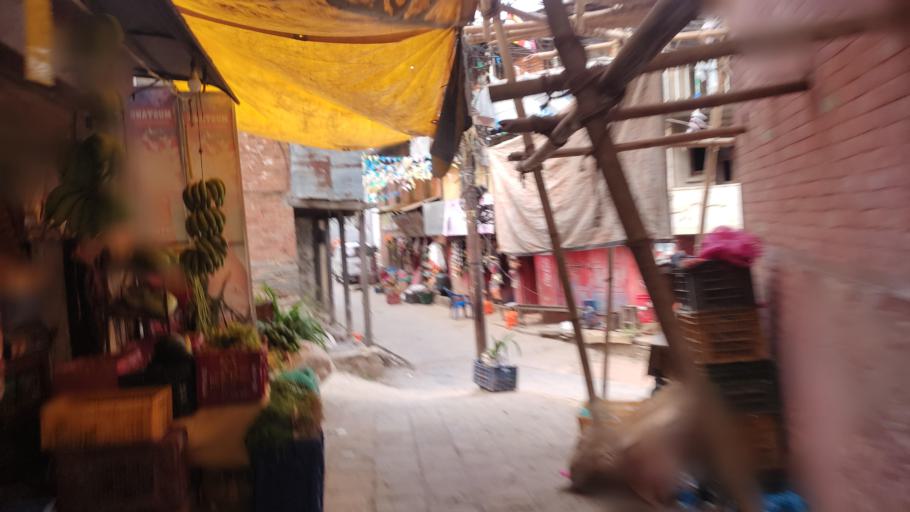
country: NP
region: Central Region
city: Kirtipur
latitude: 27.6679
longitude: 85.2493
